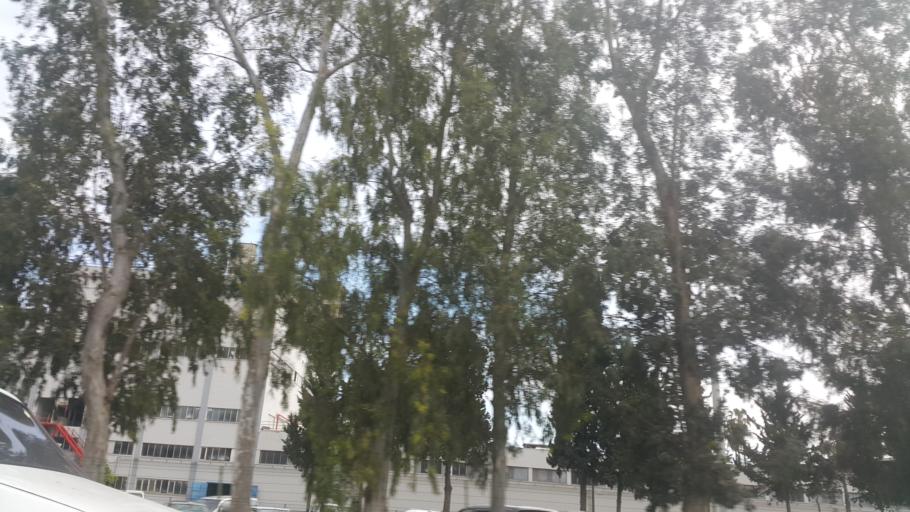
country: TR
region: Adana
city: Seyhan
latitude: 36.9934
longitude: 35.1979
